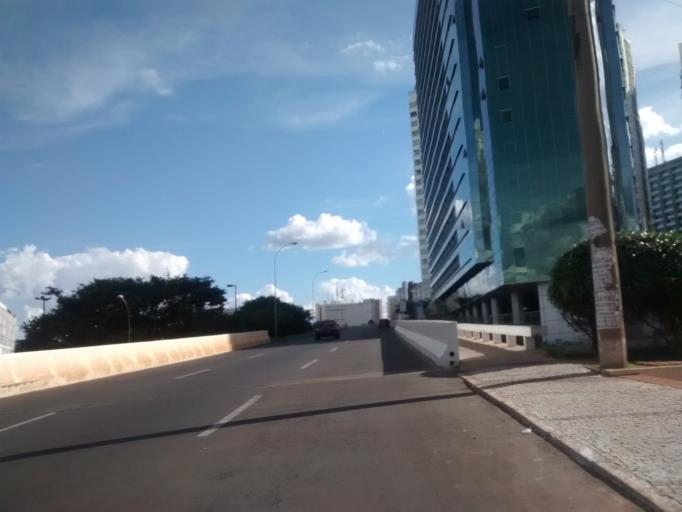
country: BR
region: Federal District
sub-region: Brasilia
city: Brasilia
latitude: -15.7896
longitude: -47.8833
